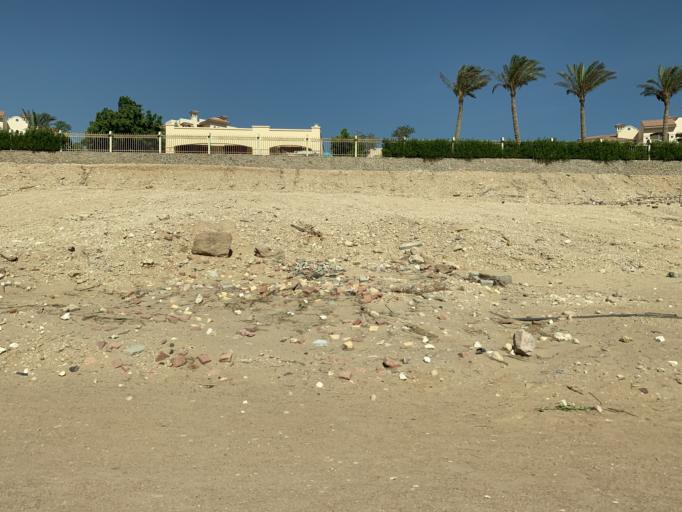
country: EG
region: As Suways
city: Ain Sukhna
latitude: 29.2225
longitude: 32.6209
